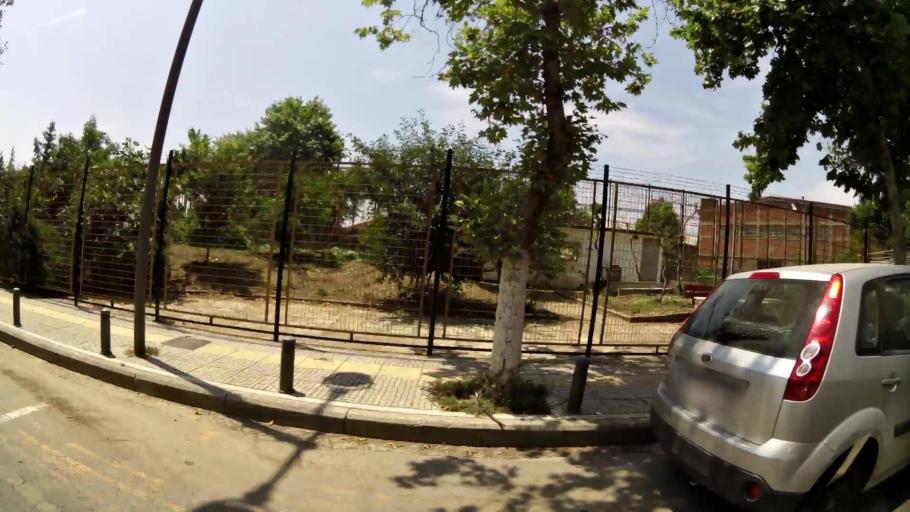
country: GR
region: Central Macedonia
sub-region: Nomos Thessalonikis
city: Ampelokipoi
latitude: 40.6540
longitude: 22.9169
